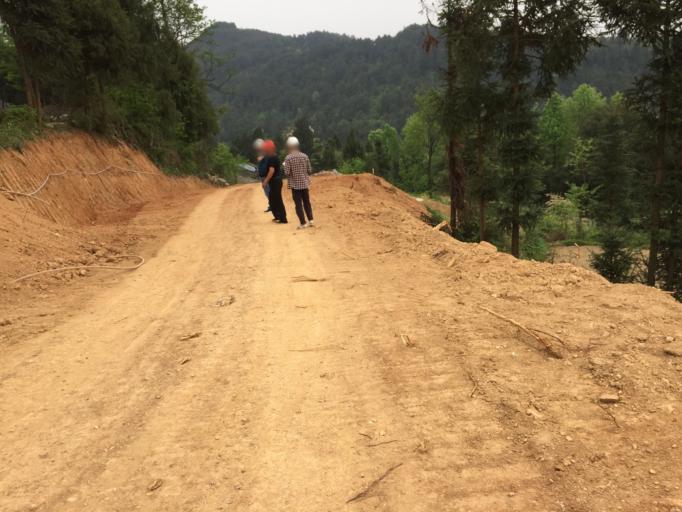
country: CN
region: Guizhou Sheng
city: Chaodi
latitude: 27.9820
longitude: 108.2210
